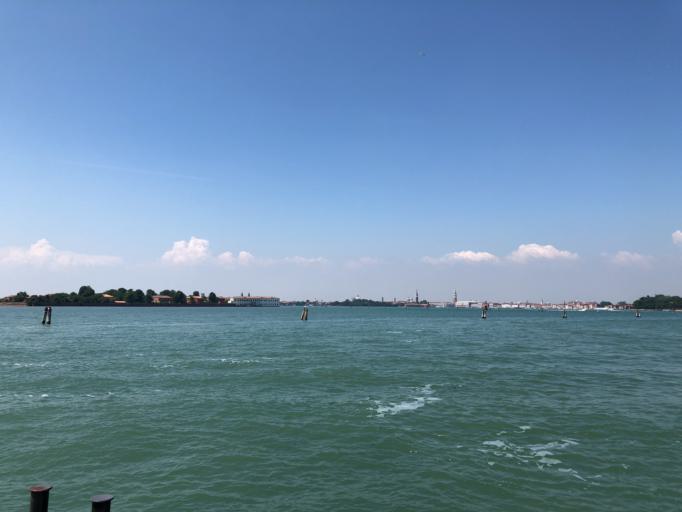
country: IT
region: Veneto
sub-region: Provincia di Venezia
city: Lido
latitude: 45.4174
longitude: 12.3675
